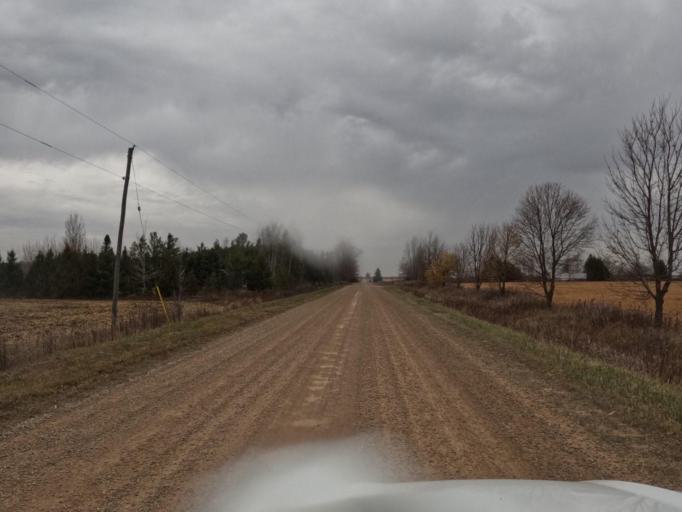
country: CA
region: Ontario
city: Shelburne
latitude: 43.8715
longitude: -80.3789
